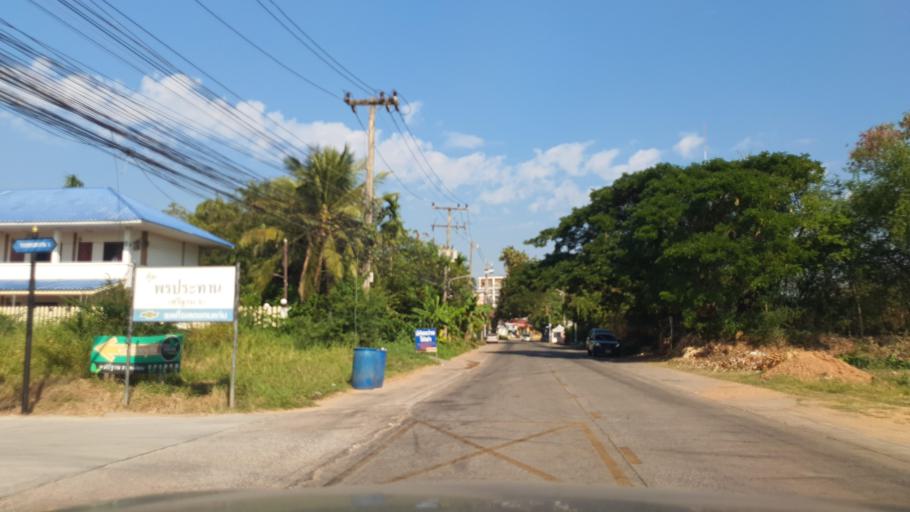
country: TH
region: Khon Kaen
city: Khon Kaen
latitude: 16.4375
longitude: 102.8139
